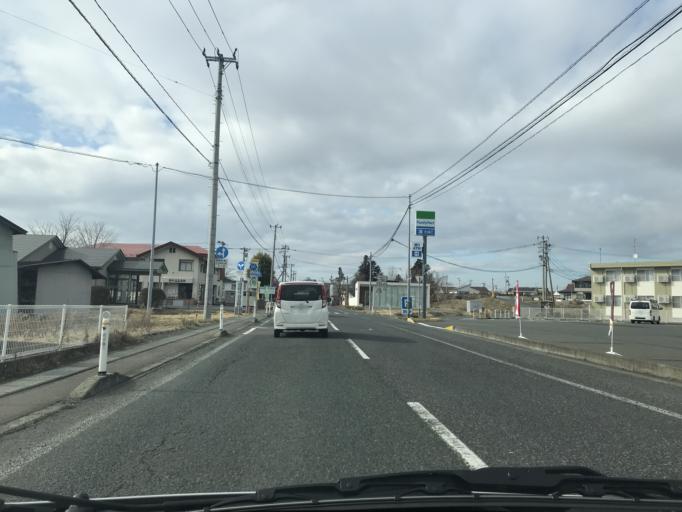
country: JP
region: Iwate
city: Hanamaki
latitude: 39.4015
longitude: 141.1185
